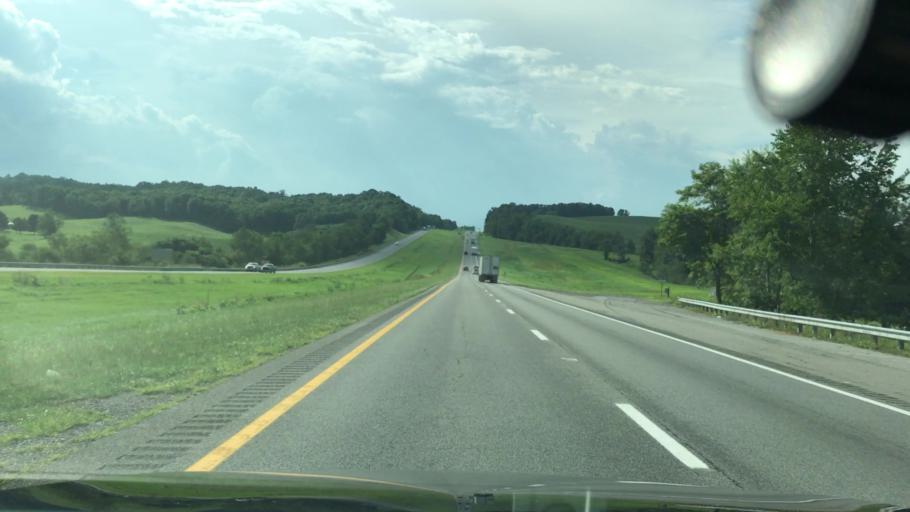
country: US
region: Virginia
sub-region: Pulaski County
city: Pulaski
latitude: 36.9091
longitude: -80.8848
